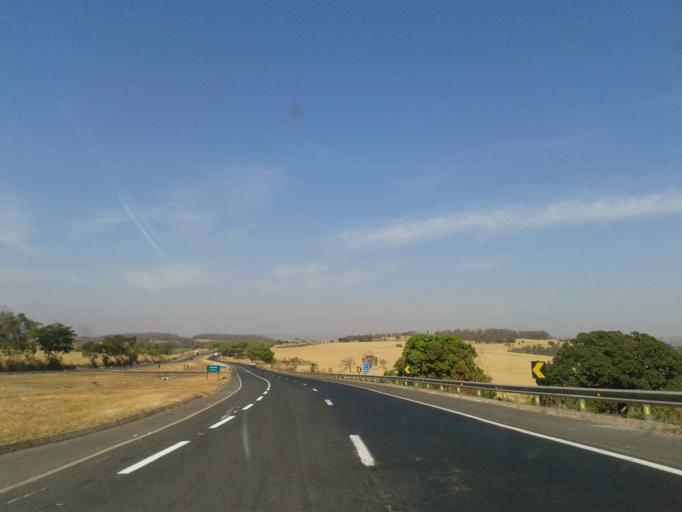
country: BR
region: Goias
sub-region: Goiatuba
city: Goiatuba
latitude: -18.0806
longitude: -49.2710
